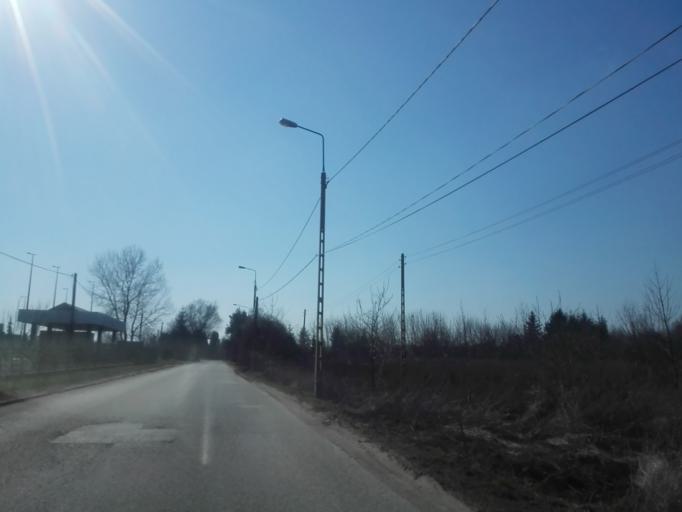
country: PL
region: Masovian Voivodeship
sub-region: Warszawa
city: Wilanow
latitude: 52.1864
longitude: 21.1002
